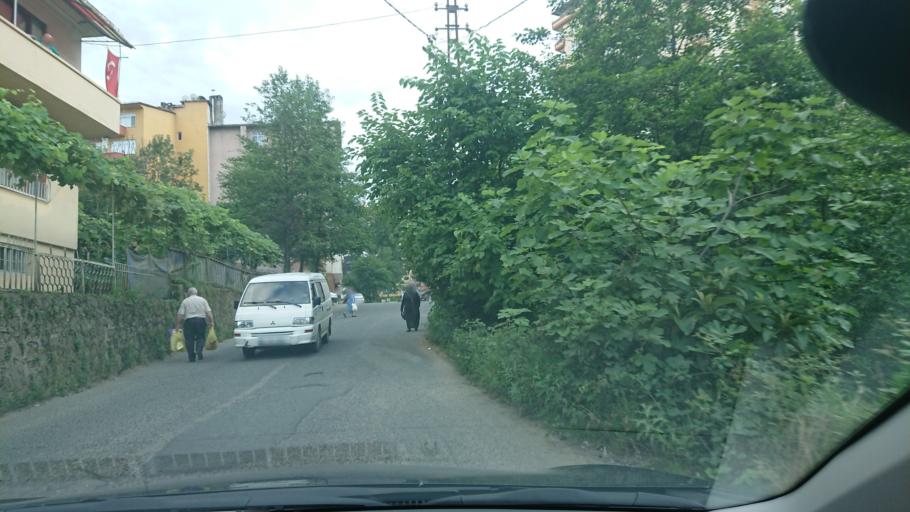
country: TR
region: Rize
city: Rize
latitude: 41.0193
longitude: 40.5165
